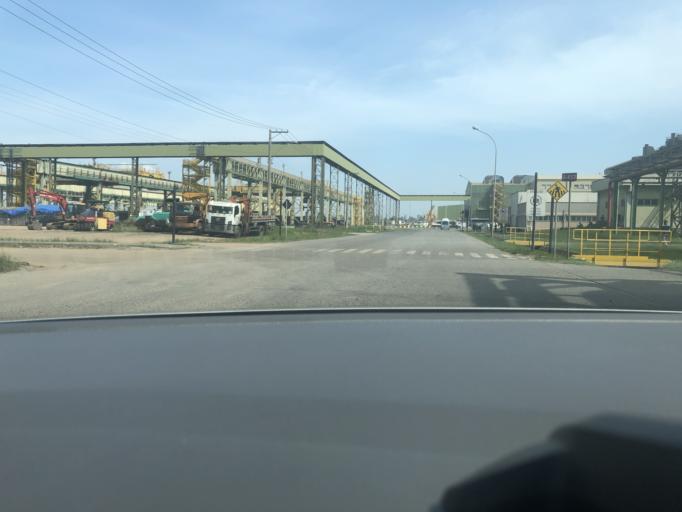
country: BR
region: Rio de Janeiro
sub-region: Itaguai
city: Itaguai
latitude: -22.9043
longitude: -43.7368
